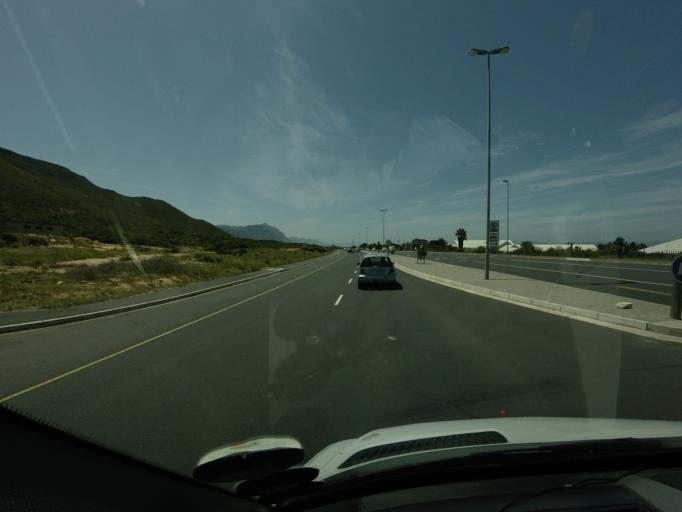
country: ZA
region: Western Cape
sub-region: Overberg District Municipality
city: Hermanus
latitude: -34.4182
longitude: 19.2192
